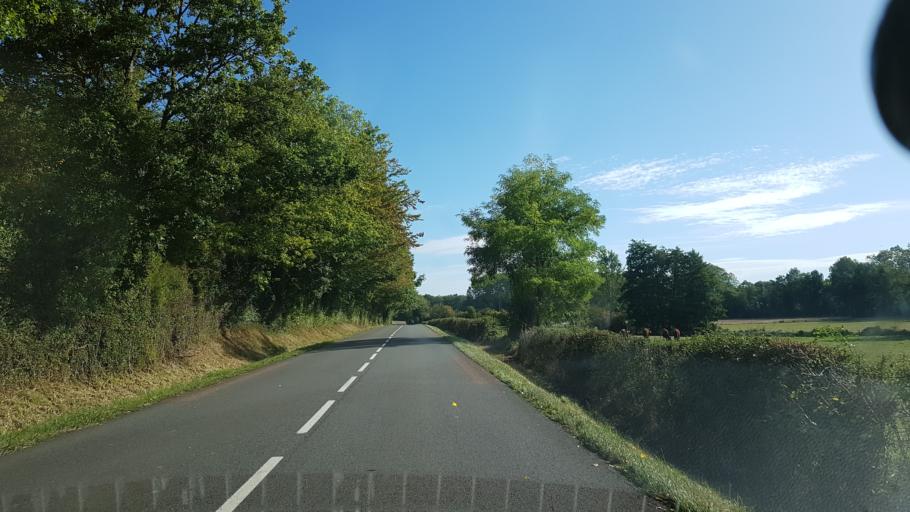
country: FR
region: Bourgogne
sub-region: Departement de la Nievre
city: Neuvy-sur-Loire
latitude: 47.5410
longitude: 2.9428
